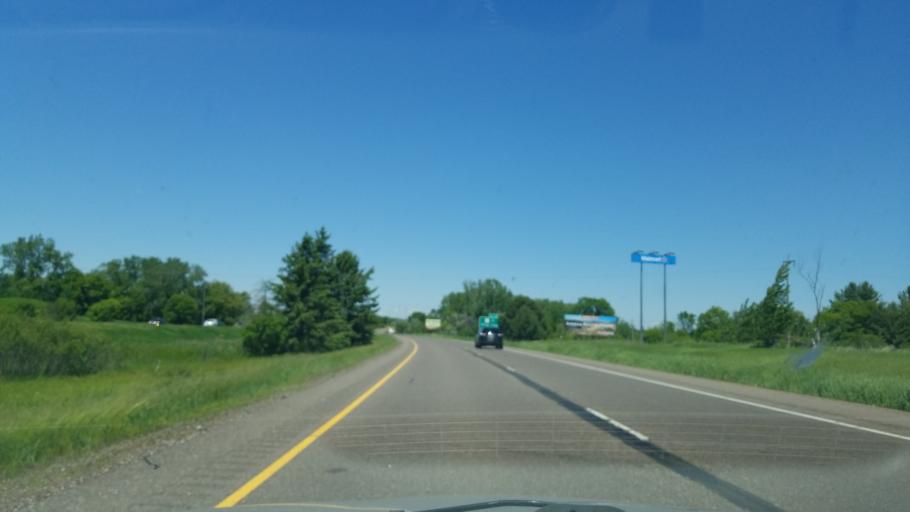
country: US
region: Minnesota
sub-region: Pine County
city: Pine City
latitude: 45.8165
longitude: -92.9837
